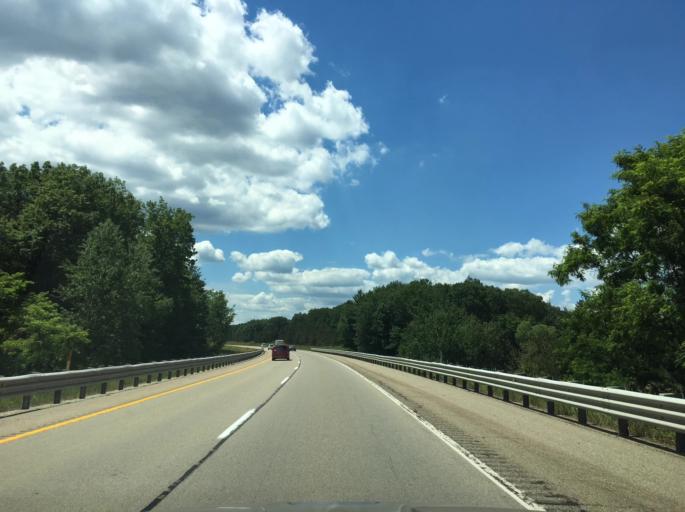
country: US
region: Michigan
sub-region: Clare County
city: Clare
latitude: 43.8830
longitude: -84.8099
